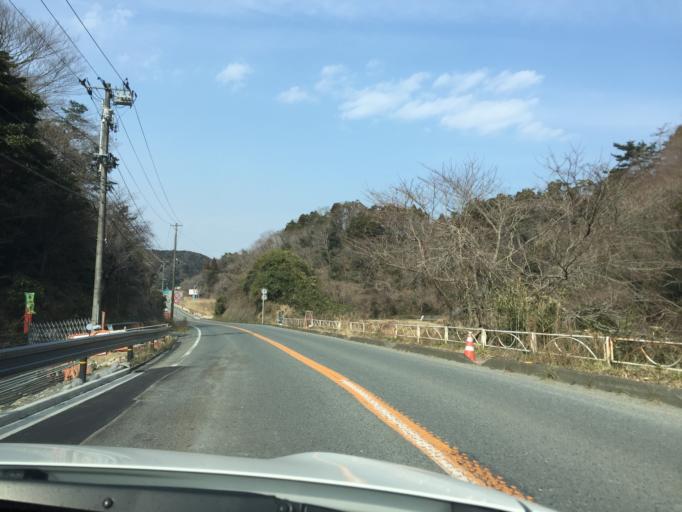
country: JP
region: Fukushima
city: Iwaki
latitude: 37.0016
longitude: 140.9675
